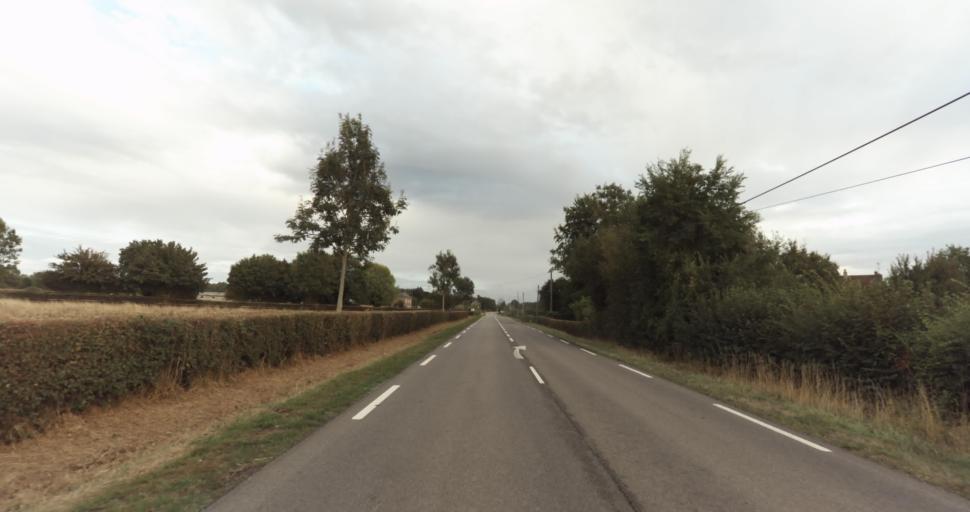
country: FR
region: Lower Normandy
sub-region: Departement de l'Orne
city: Vimoutiers
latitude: 48.9177
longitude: 0.2347
